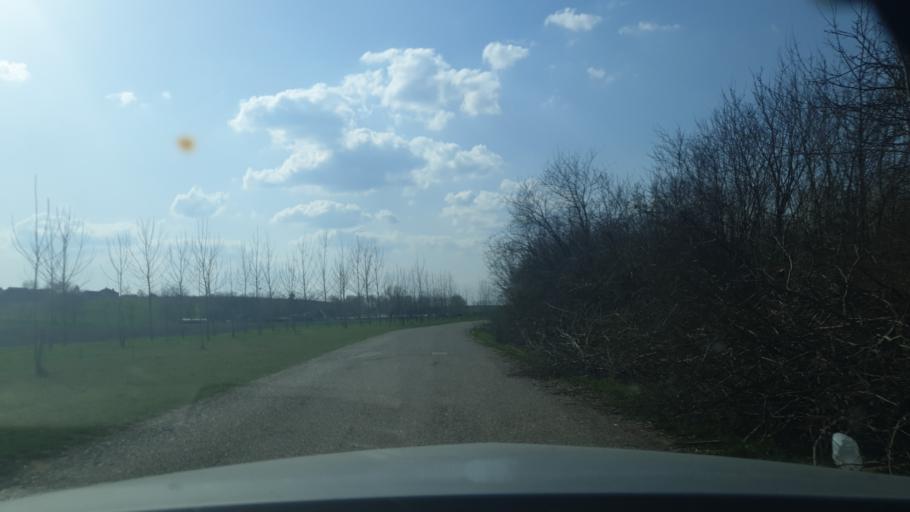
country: RS
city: Putinci
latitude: 45.0081
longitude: 19.9419
